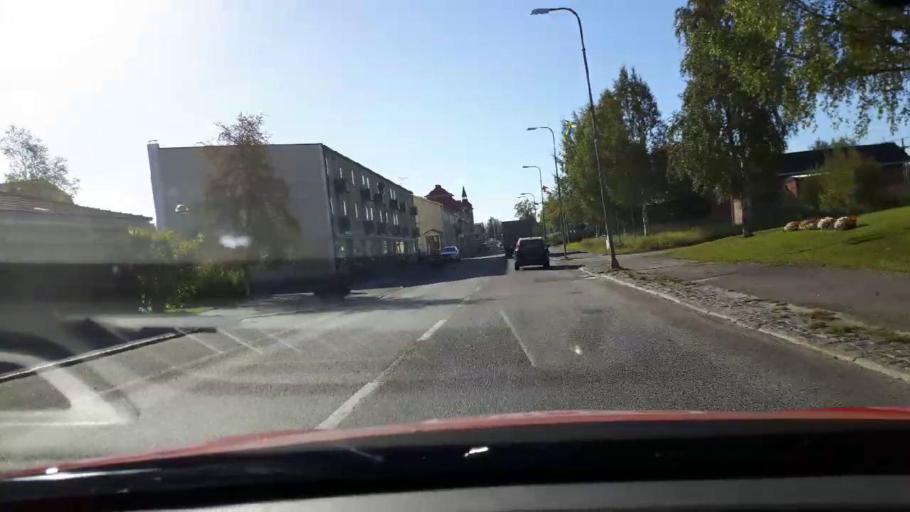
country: SE
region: Jaemtland
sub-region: Braecke Kommun
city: Braecke
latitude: 62.7526
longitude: 15.4169
